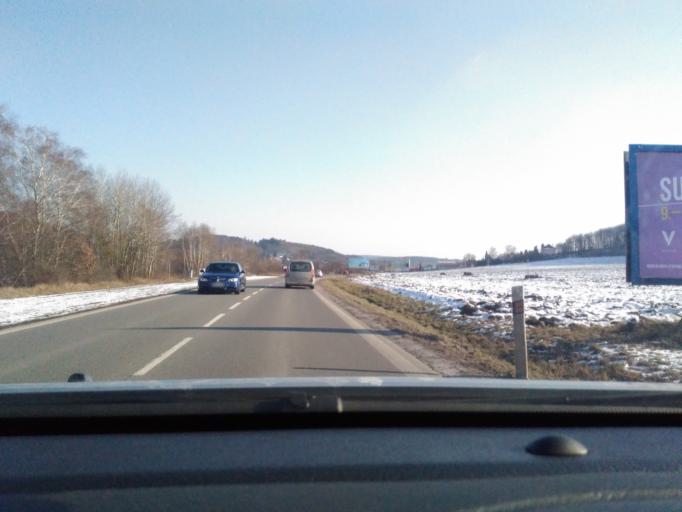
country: CZ
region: South Moravian
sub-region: Okres Brno-Venkov
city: Lelekovice
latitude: 49.2929
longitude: 16.5566
